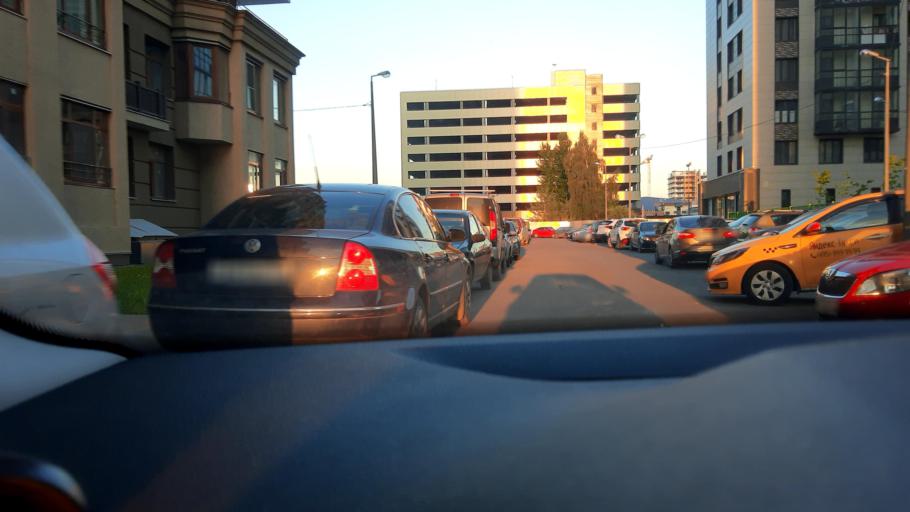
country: RU
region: Moscow
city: Khimki
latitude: 55.9146
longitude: 37.4088
